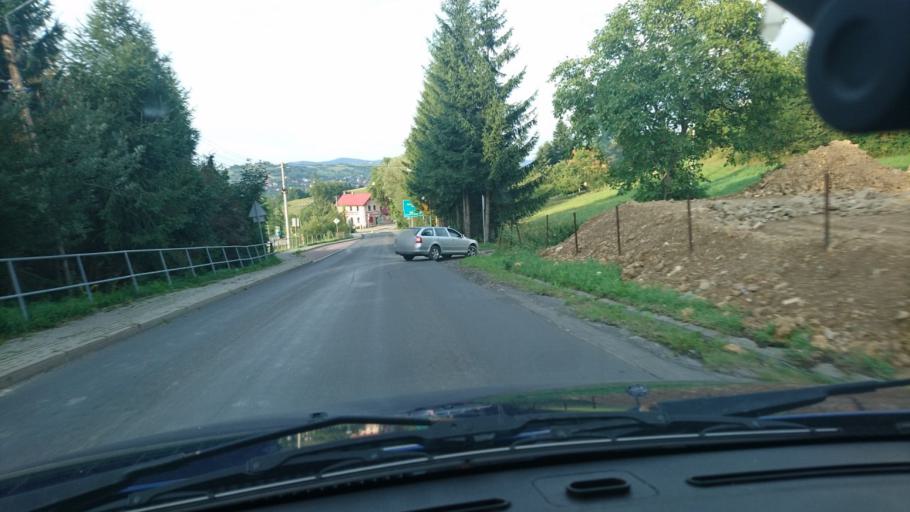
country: PL
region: Silesian Voivodeship
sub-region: Powiat cieszynski
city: Jaworzynka
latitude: 49.5488
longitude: 18.8817
